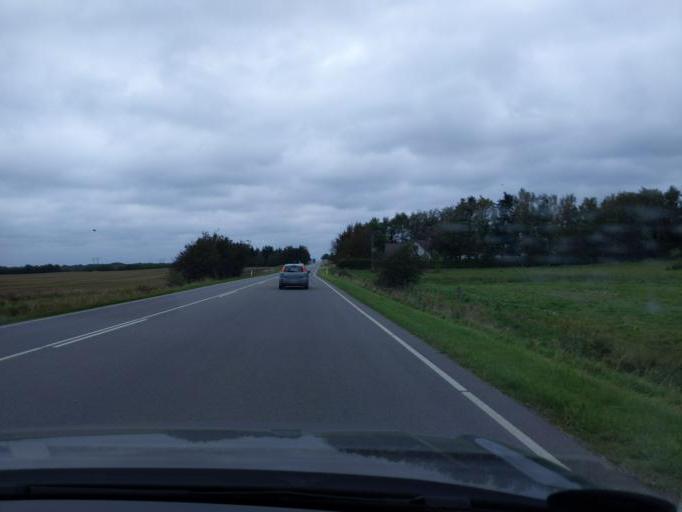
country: DK
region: North Denmark
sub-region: Mariagerfjord Kommune
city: Hobro
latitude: 56.5749
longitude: 9.8155
